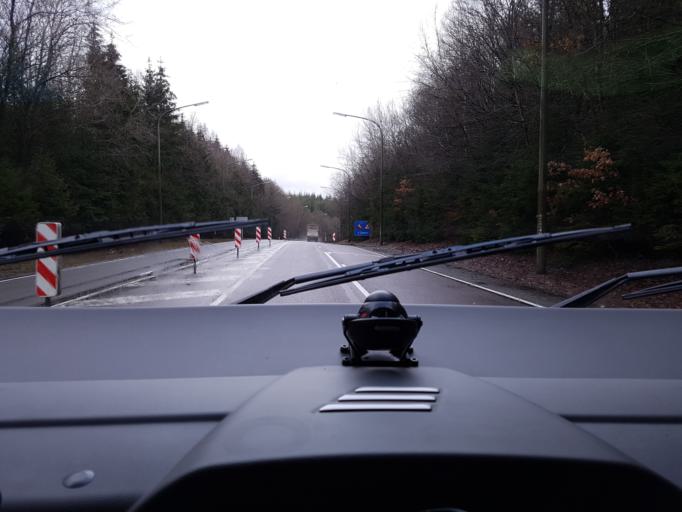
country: BE
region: Wallonia
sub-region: Province du Luxembourg
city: Martelange
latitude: 49.8105
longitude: 5.7388
